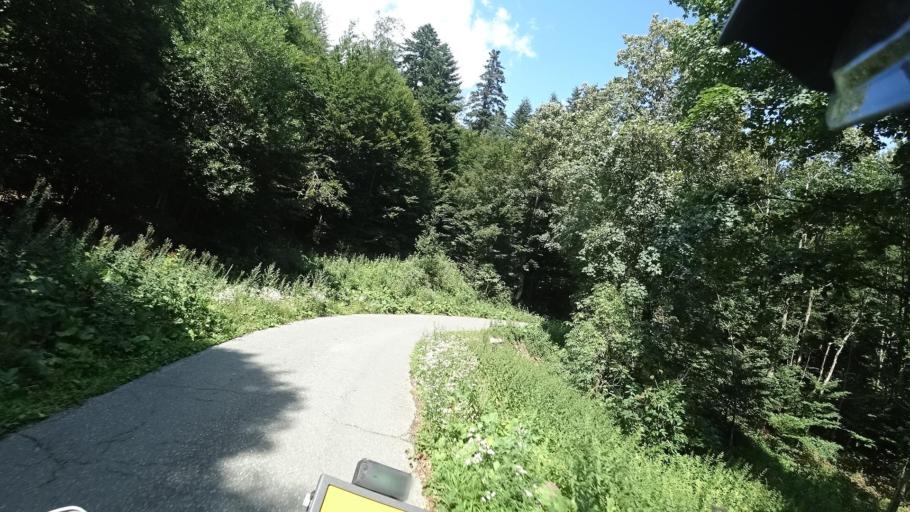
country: HR
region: Licko-Senjska
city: Brinje
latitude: 45.1069
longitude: 15.0278
